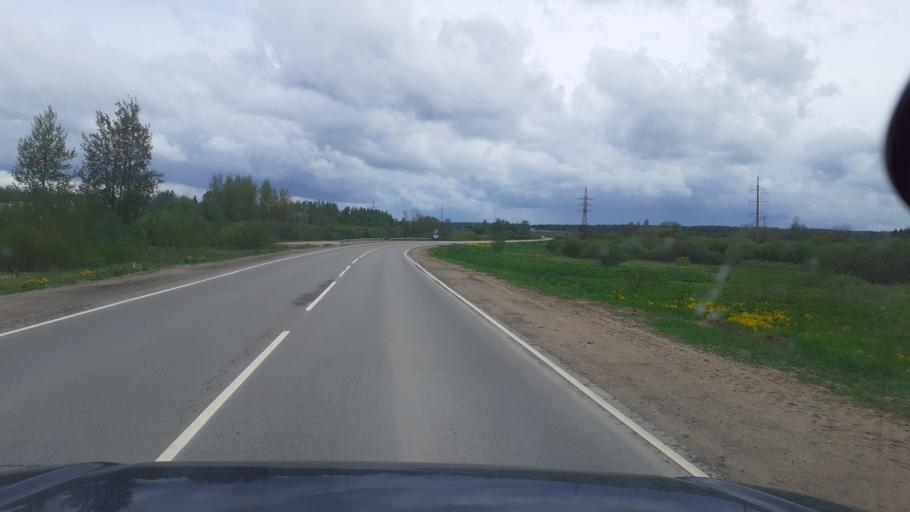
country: RU
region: Moskovskaya
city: Sychevo
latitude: 55.9866
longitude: 36.2210
